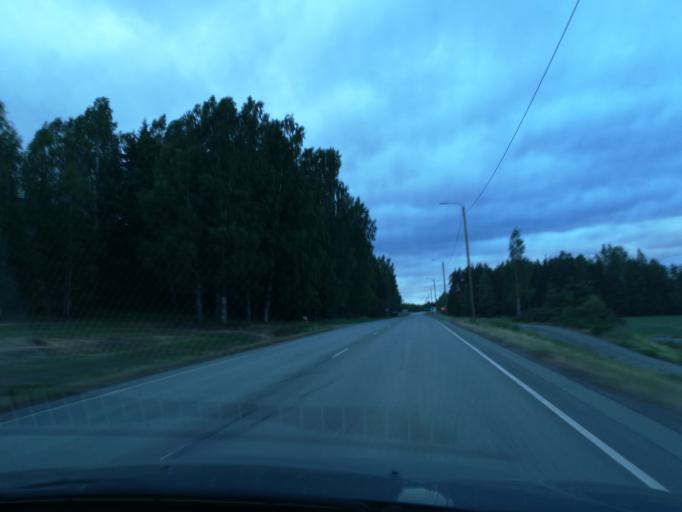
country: FI
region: Southern Savonia
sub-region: Mikkeli
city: Ristiina
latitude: 61.4955
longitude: 27.2416
